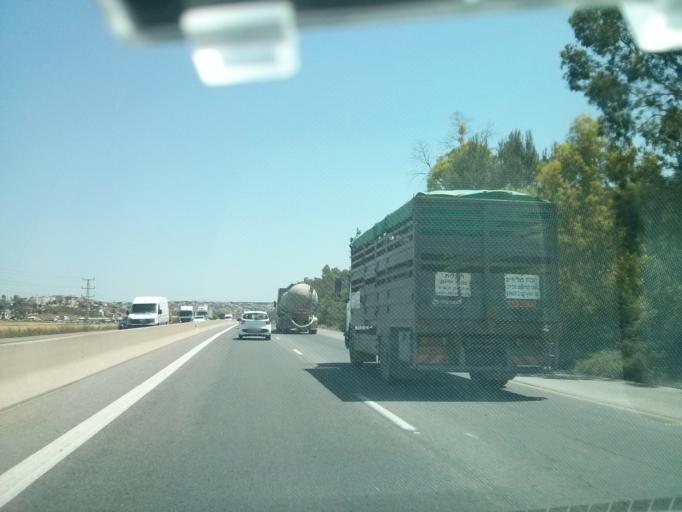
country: PS
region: West Bank
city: Barta`ah ash Sharqiyah
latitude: 32.4923
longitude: 35.0554
